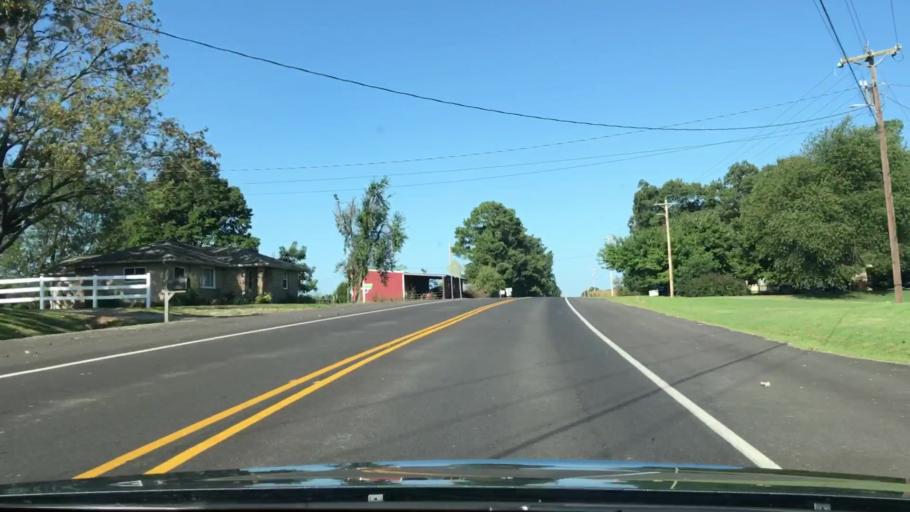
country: US
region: Kentucky
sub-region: Marshall County
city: Benton
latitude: 36.7647
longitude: -88.3146
